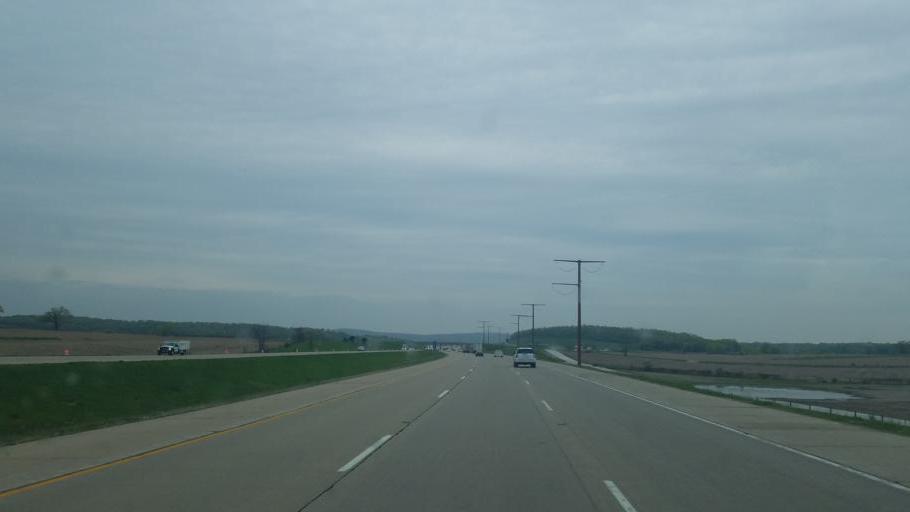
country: US
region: Wisconsin
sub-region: Columbia County
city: Poynette
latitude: 43.4152
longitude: -89.4698
